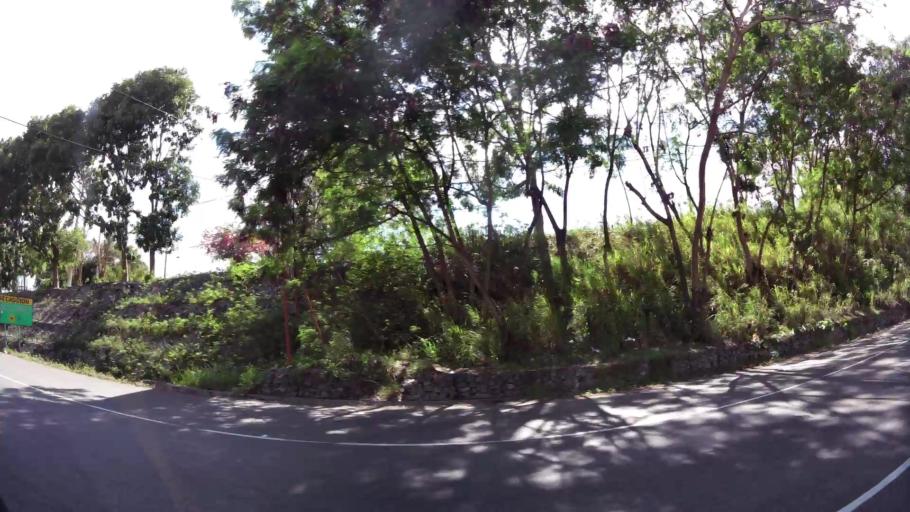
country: DO
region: Santo Domingo
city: Santo Domingo Oeste
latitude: 18.5583
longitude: -70.0586
